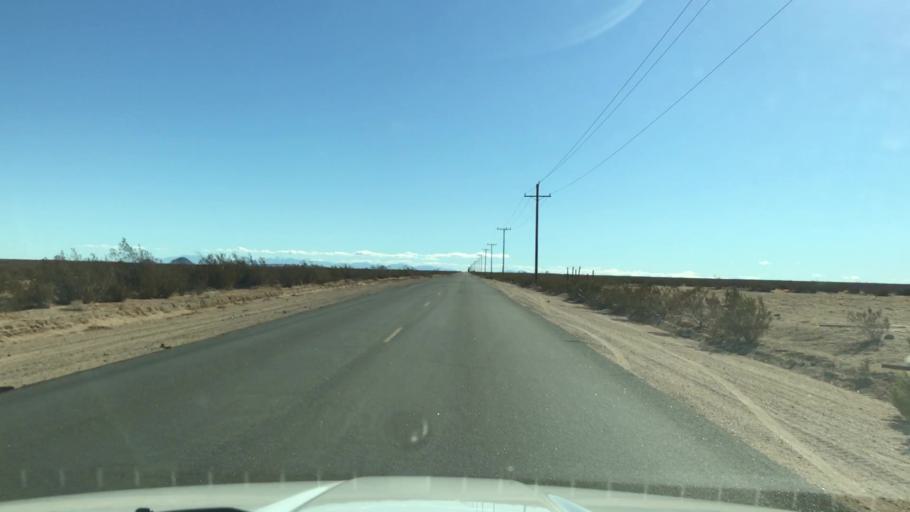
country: US
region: California
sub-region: Kern County
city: California City
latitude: 35.2049
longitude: -117.9859
